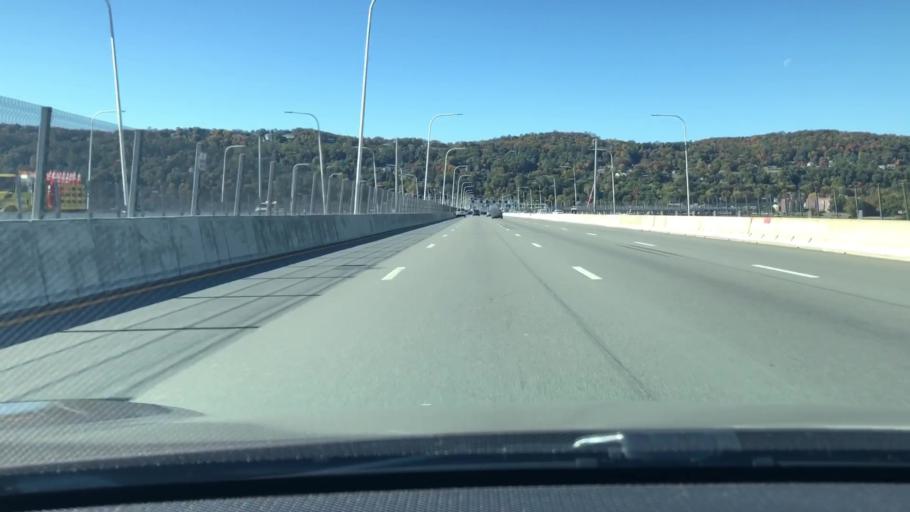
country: US
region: New York
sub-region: Rockland County
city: South Nyack
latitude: 41.0712
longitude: -73.9022
